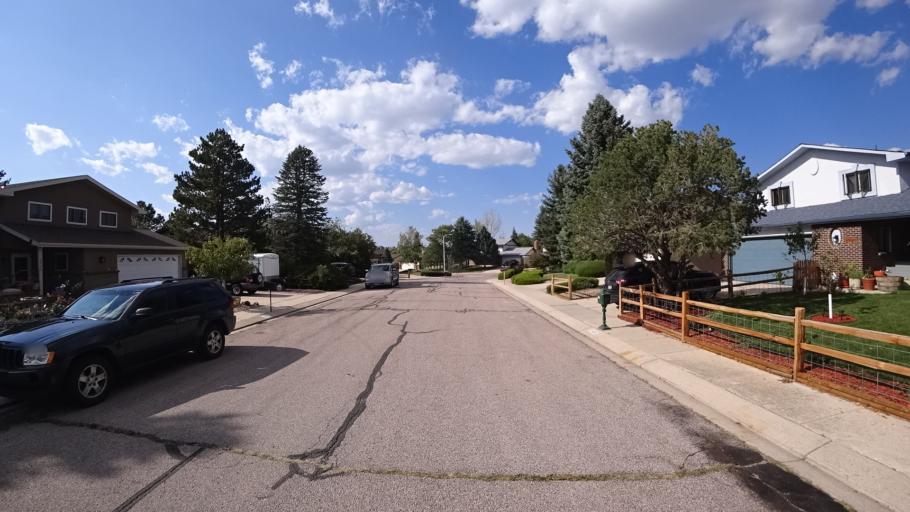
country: US
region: Colorado
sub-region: El Paso County
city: Cimarron Hills
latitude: 38.8743
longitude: -104.7297
